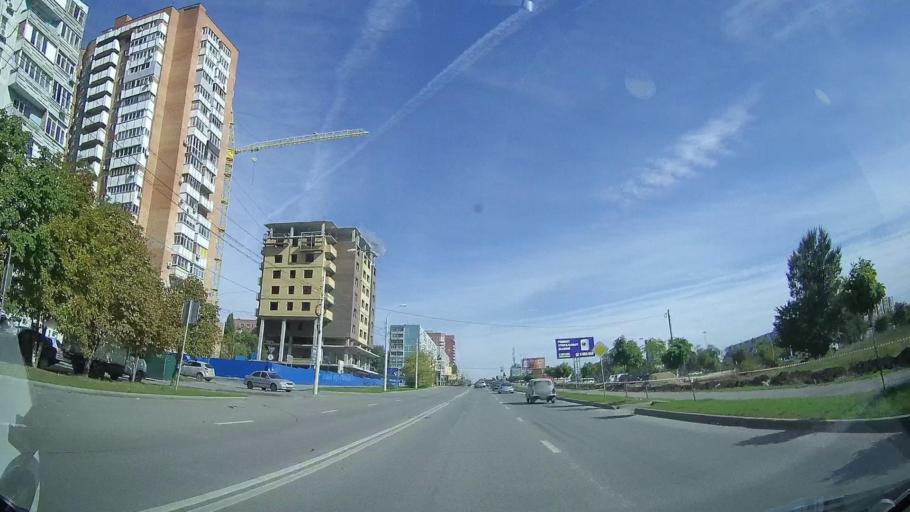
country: RU
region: Rostov
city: Severnyy
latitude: 47.2887
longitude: 39.7016
